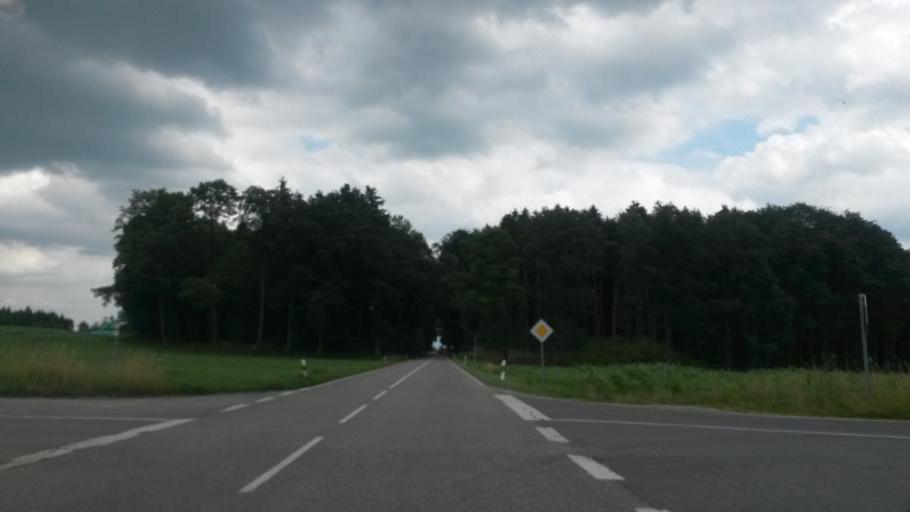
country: DE
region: Bavaria
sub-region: Upper Bavaria
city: Bad Endorf
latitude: 47.9103
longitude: 12.3189
